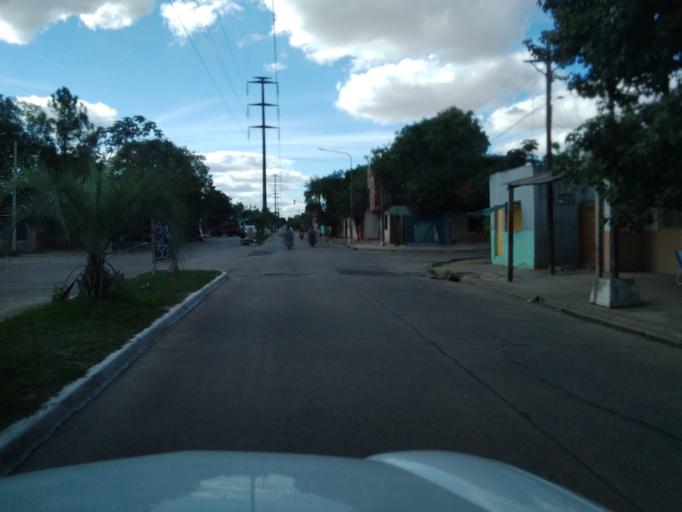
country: AR
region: Corrientes
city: Corrientes
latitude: -27.4901
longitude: -58.8382
